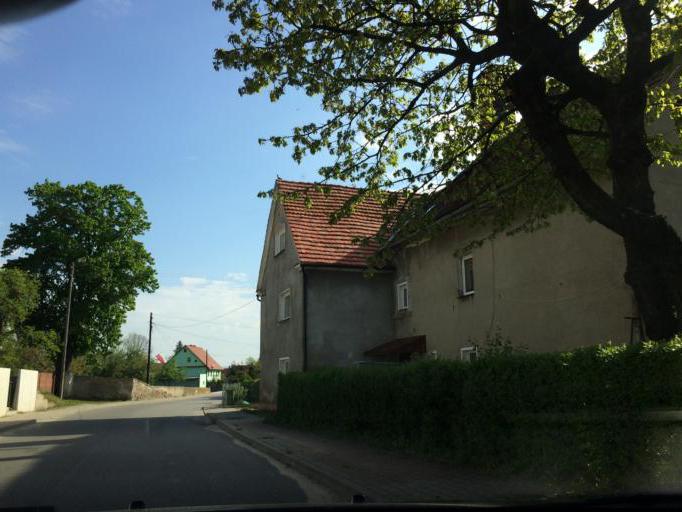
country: PL
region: Lower Silesian Voivodeship
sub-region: Powiat dzierzoniowski
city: Pieszyce
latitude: 50.7559
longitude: 16.5322
